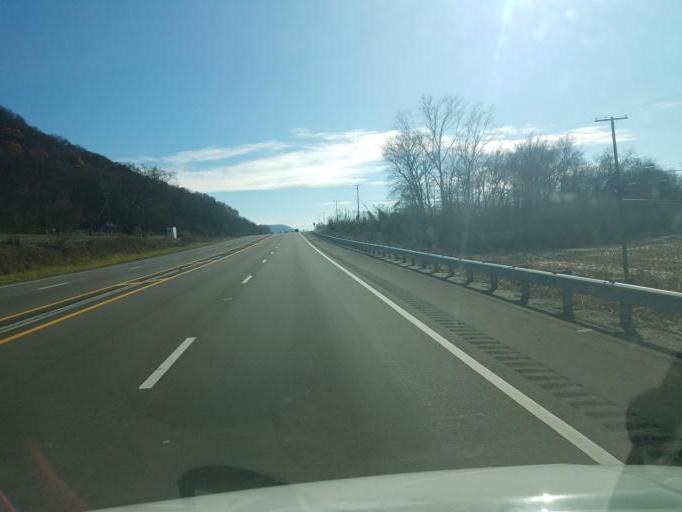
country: US
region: Ohio
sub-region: Scioto County
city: Lucasville
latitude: 38.8536
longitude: -82.9870
